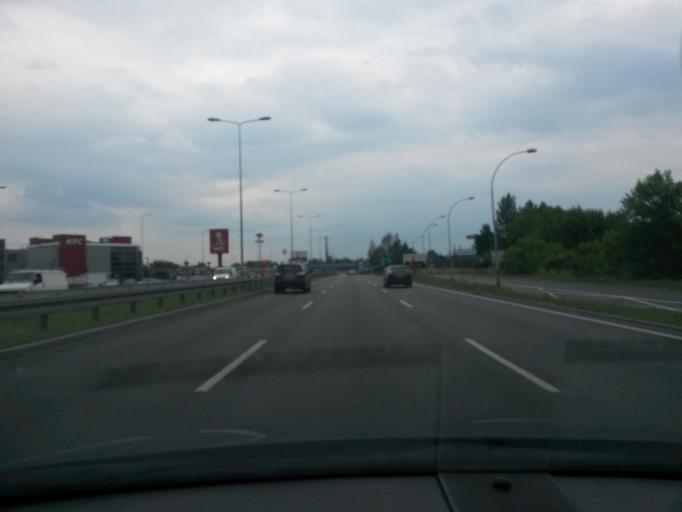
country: PL
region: Silesian Voivodeship
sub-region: Czestochowa
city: Czestochowa
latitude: 50.8226
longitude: 19.1411
